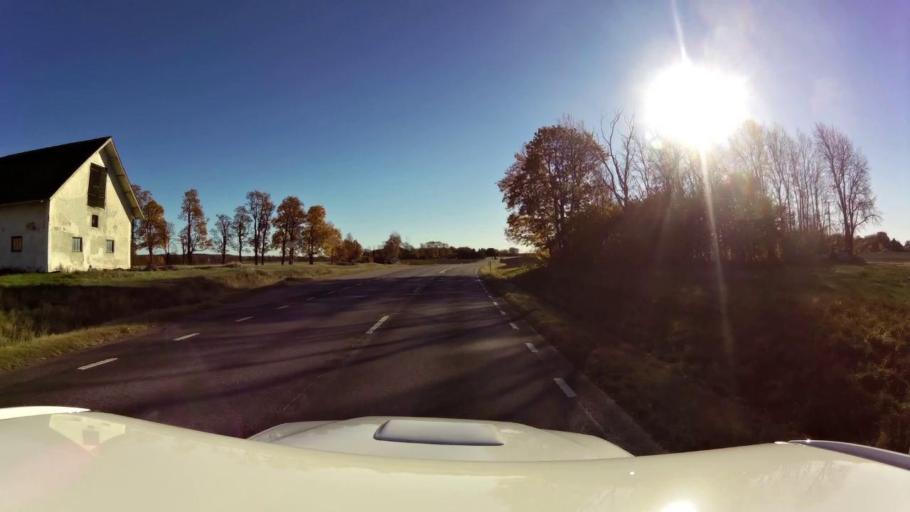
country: SE
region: OEstergoetland
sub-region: Linkopings Kommun
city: Ljungsbro
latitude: 58.5285
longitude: 15.4084
